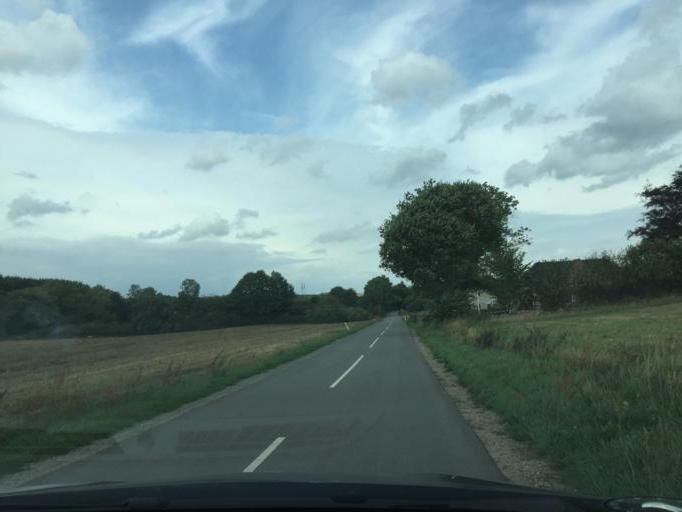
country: DK
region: South Denmark
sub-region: Assens Kommune
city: Tommerup Stationsby
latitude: 55.3715
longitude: 10.1693
